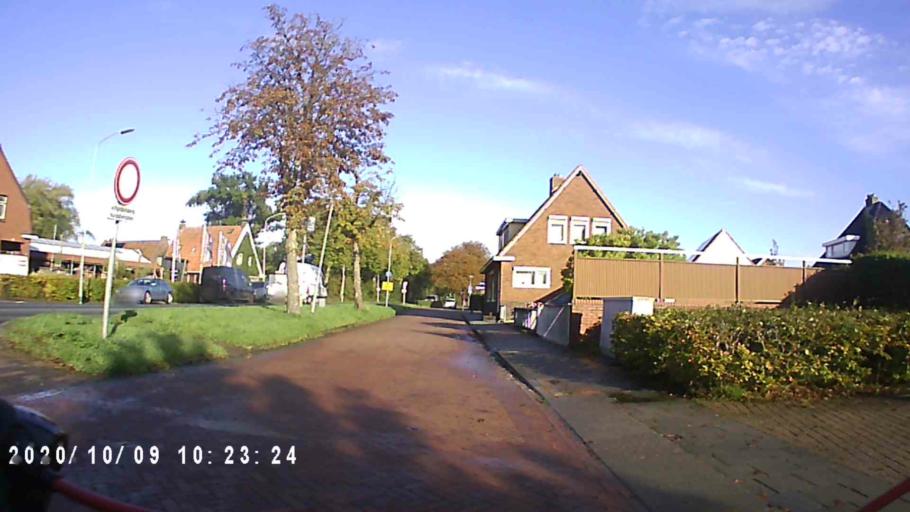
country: NL
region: Groningen
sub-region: Gemeente Winsum
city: Winsum
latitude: 53.3276
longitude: 6.5137
